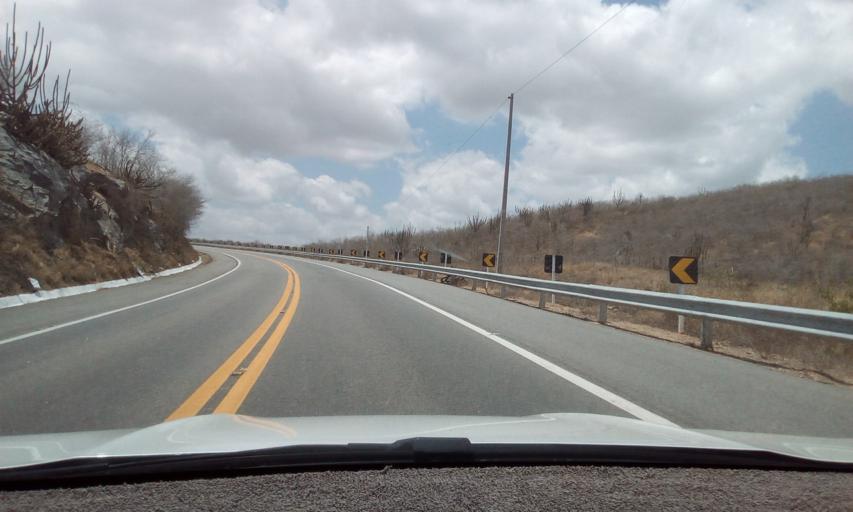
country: BR
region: Paraiba
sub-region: Boqueirao
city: Boqueirao
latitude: -7.6693
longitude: -36.0809
